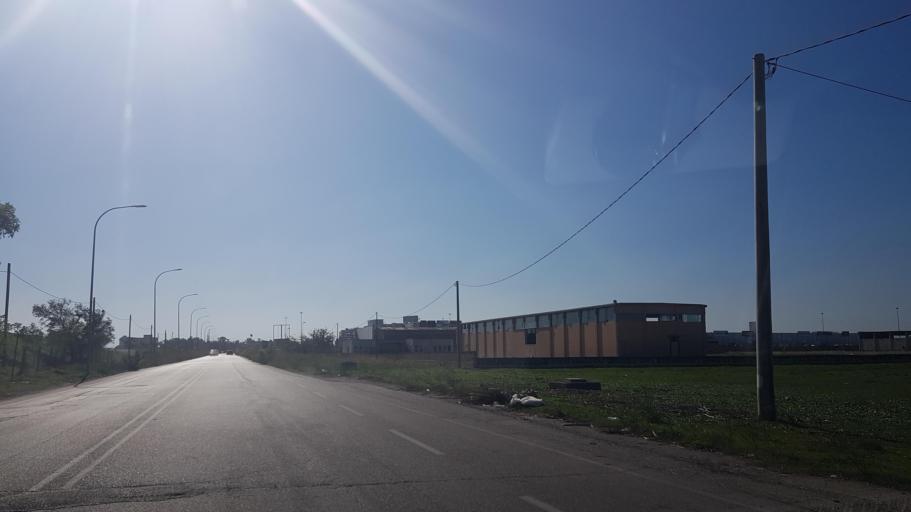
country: IT
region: Apulia
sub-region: Provincia di Foggia
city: Carapelle
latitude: 41.4191
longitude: 15.6561
